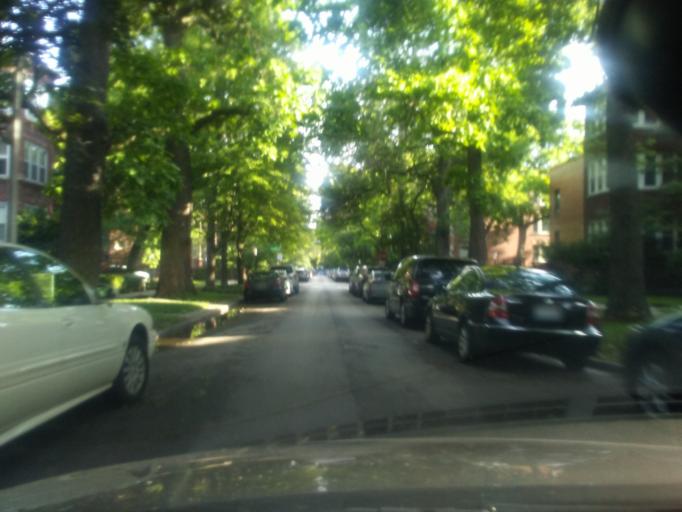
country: US
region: Illinois
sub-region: Cook County
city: Evanston
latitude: 41.9886
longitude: -87.6615
